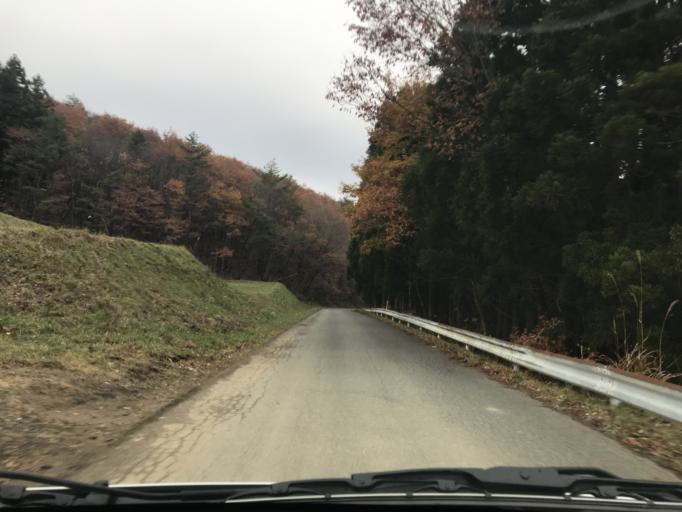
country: JP
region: Iwate
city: Ichinoseki
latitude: 39.0035
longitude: 141.0281
